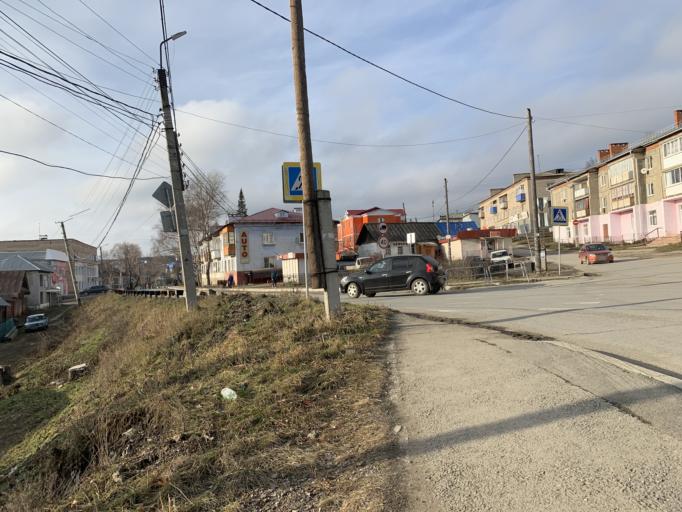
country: RU
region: Chelyabinsk
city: Nyazepetrovsk
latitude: 56.0534
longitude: 59.6024
